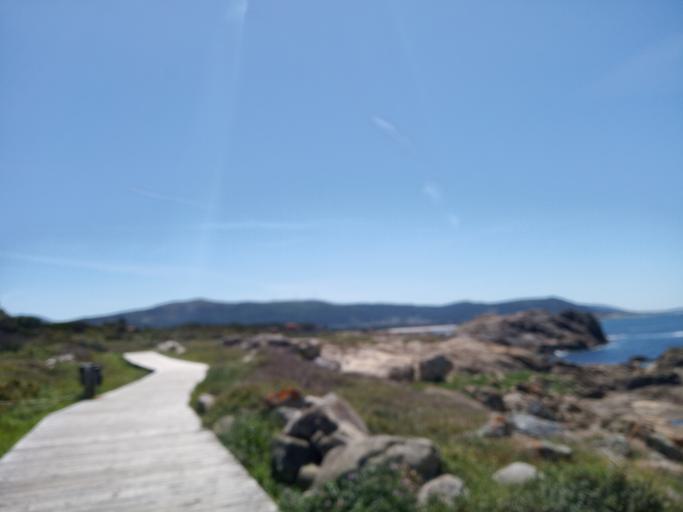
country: ES
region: Galicia
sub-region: Provincia de Pontevedra
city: A Guarda
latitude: 41.8780
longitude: -8.8789
